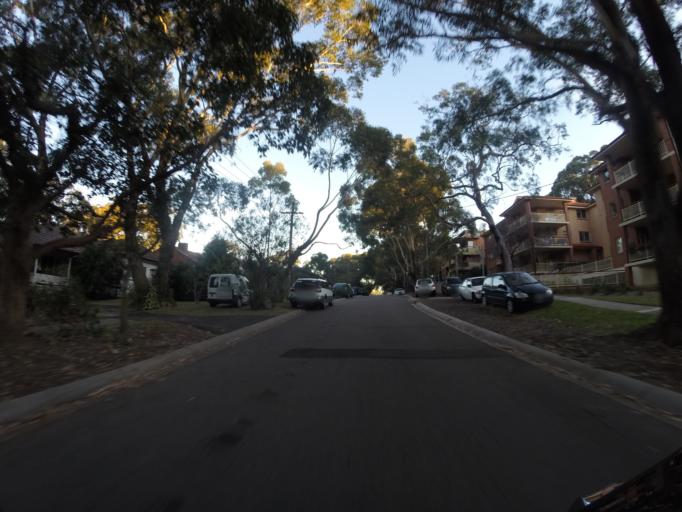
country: AU
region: New South Wales
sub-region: Sutherland Shire
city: Gymea
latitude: -34.0365
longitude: 151.0871
